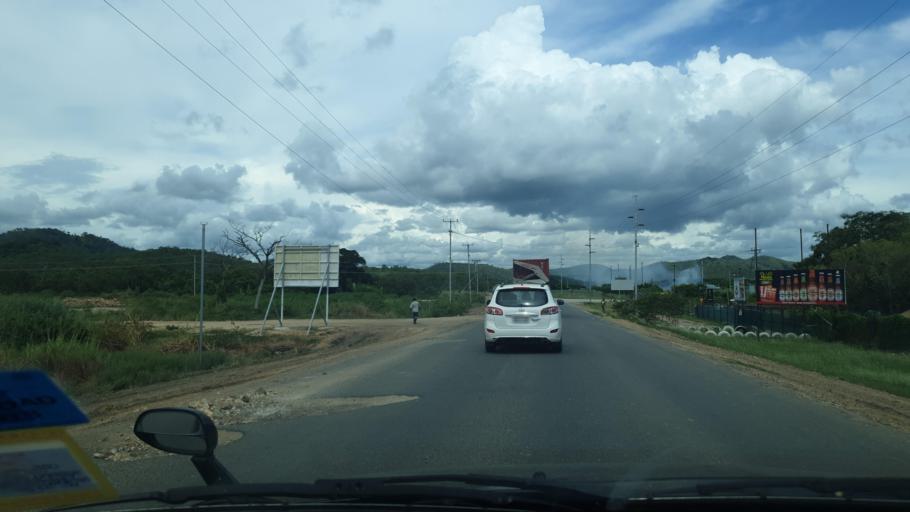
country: PG
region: National Capital
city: Port Moresby
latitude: -9.4163
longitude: 147.1102
